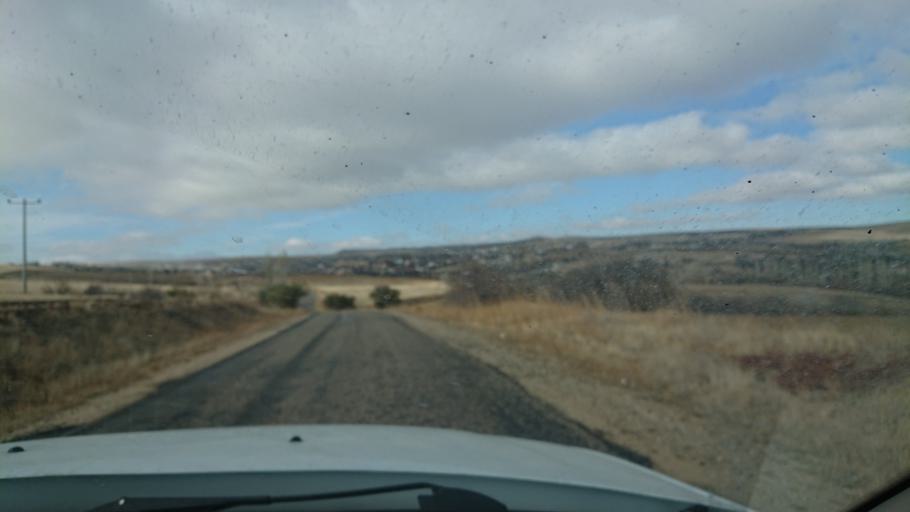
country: TR
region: Aksaray
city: Agacoren
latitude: 38.8207
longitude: 33.9741
